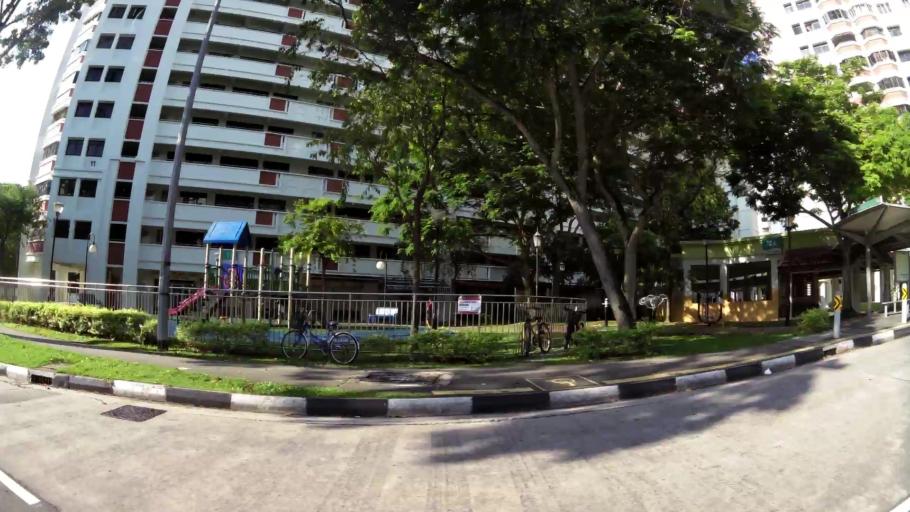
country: SG
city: Singapore
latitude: 1.3271
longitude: 103.9252
